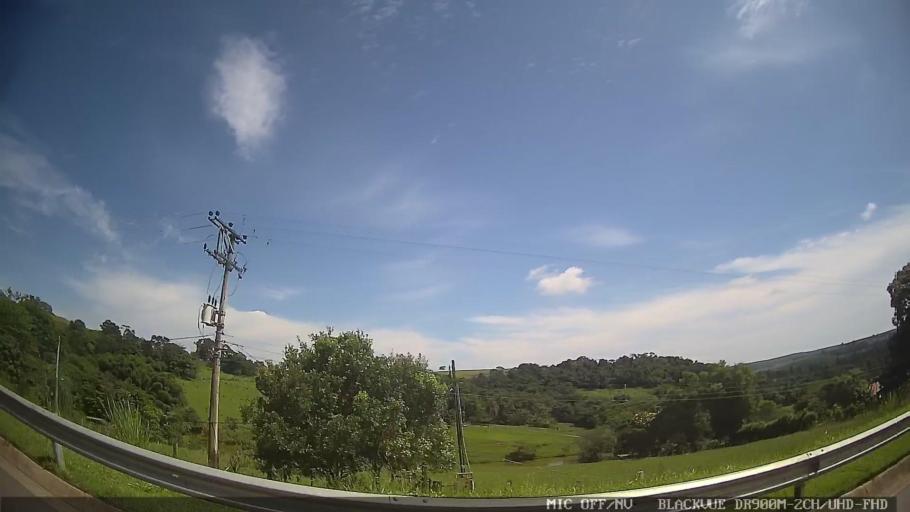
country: BR
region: Sao Paulo
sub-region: Porto Feliz
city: Porto Feliz
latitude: -23.2104
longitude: -47.5905
